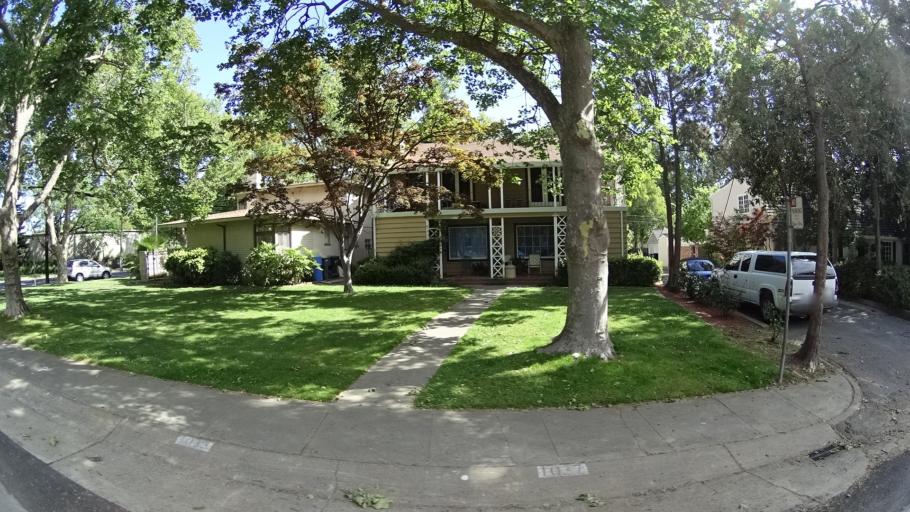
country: US
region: California
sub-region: Sacramento County
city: Sacramento
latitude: 38.5472
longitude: -121.5072
